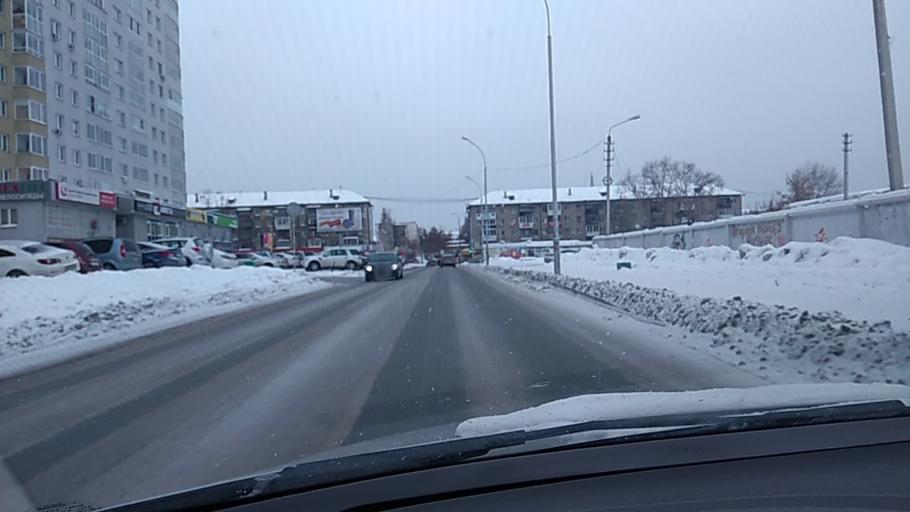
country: RU
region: Sverdlovsk
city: Yekaterinburg
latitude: 56.8069
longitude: 60.6078
